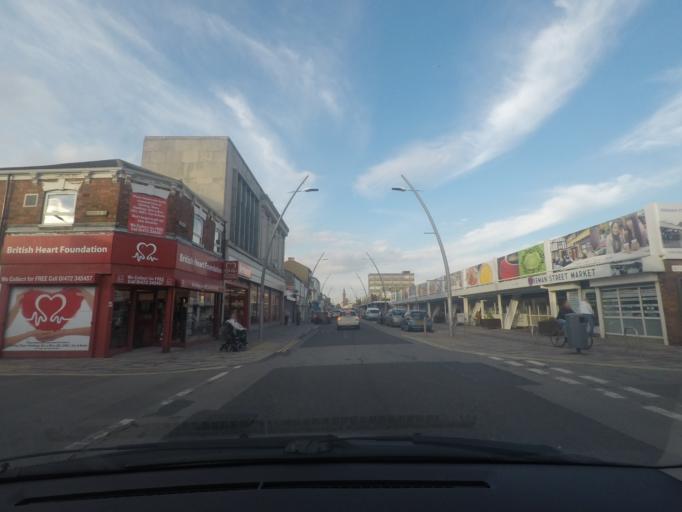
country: GB
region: England
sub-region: North East Lincolnshire
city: Grimsby
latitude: 53.5712
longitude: -0.0737
